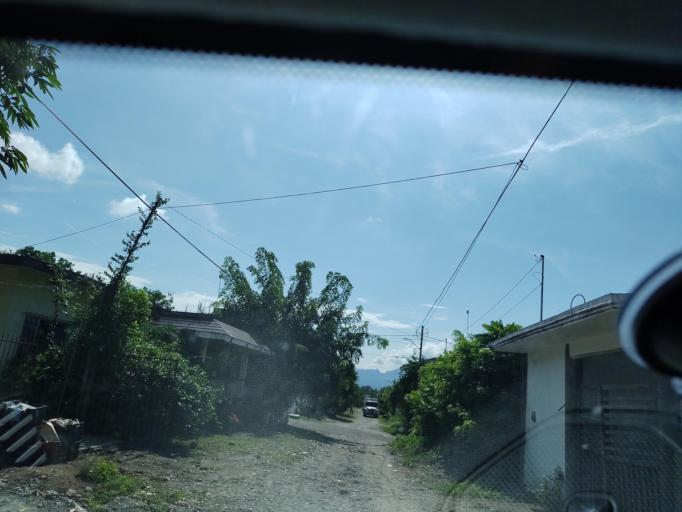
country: MX
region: Veracruz
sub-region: Martinez de la Torre
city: El Progreso
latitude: 20.1159
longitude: -97.0135
